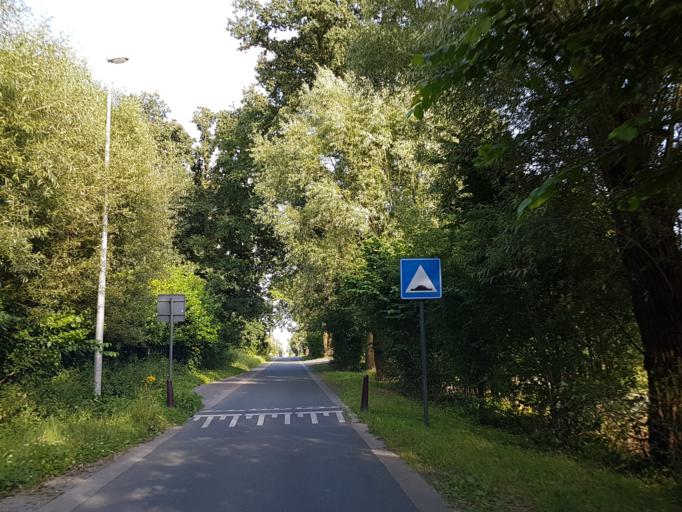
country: BE
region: Flanders
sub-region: Provincie Oost-Vlaanderen
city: Denderleeuw
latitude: 50.9342
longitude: 4.0913
